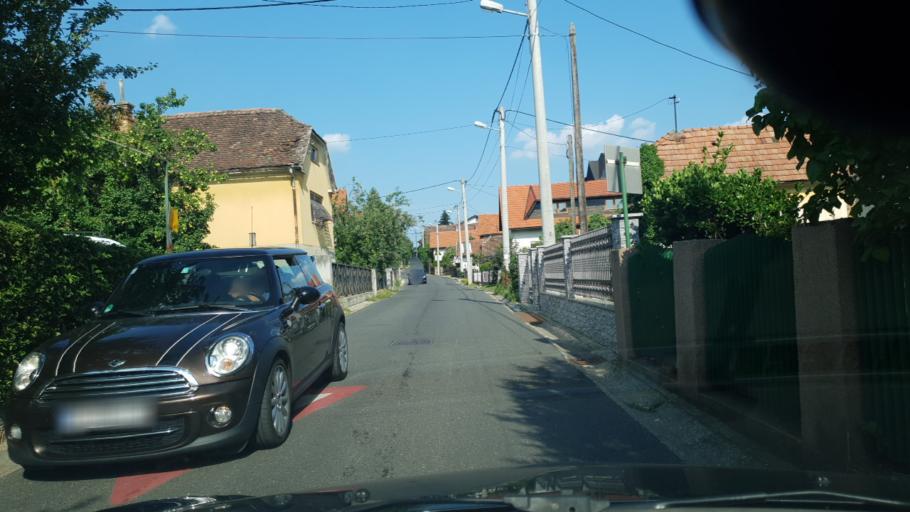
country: HR
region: Grad Zagreb
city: Zagreb
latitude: 45.8604
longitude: 15.9762
